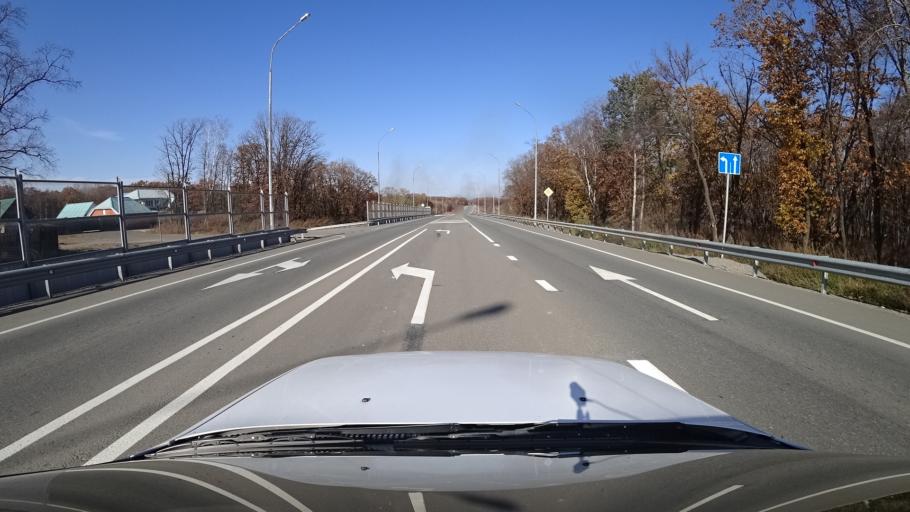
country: RU
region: Primorskiy
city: Dal'nerechensk
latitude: 45.8827
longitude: 133.7294
